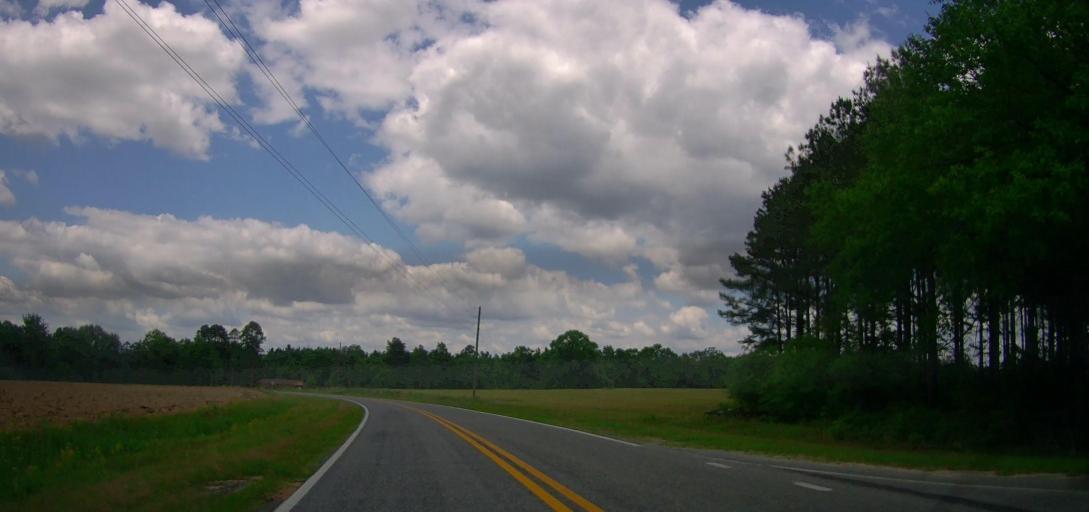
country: US
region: Georgia
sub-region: Laurens County
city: East Dublin
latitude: 32.5374
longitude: -82.8101
